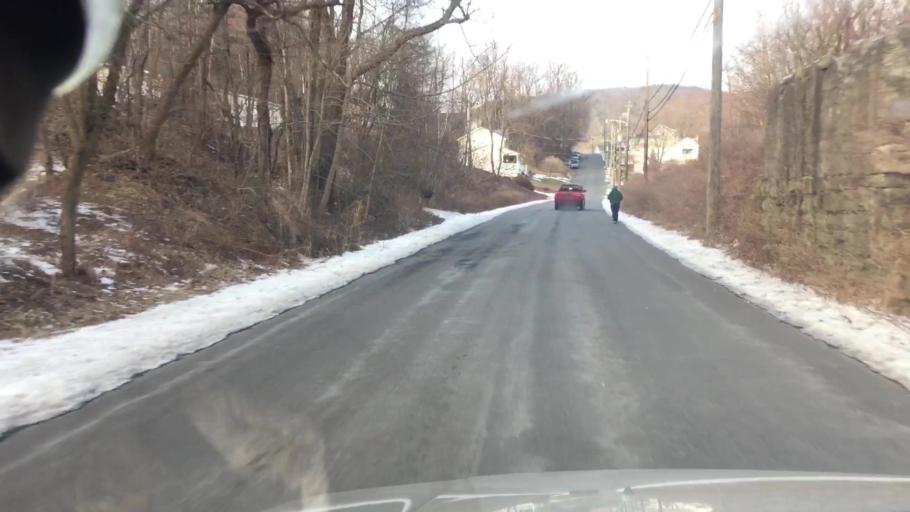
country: US
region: Pennsylvania
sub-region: Luzerne County
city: Nanticoke
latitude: 41.2071
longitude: -76.0101
